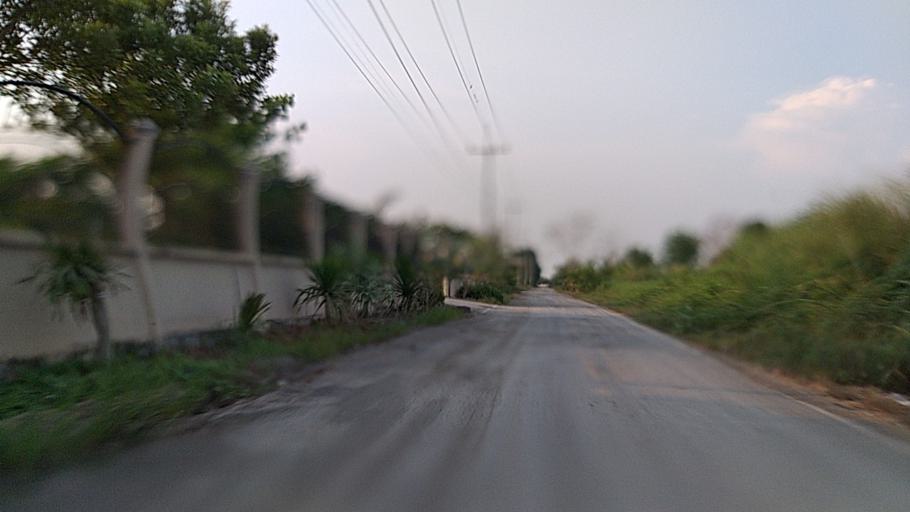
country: TH
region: Pathum Thani
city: Nong Suea
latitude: 14.0622
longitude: 100.8312
